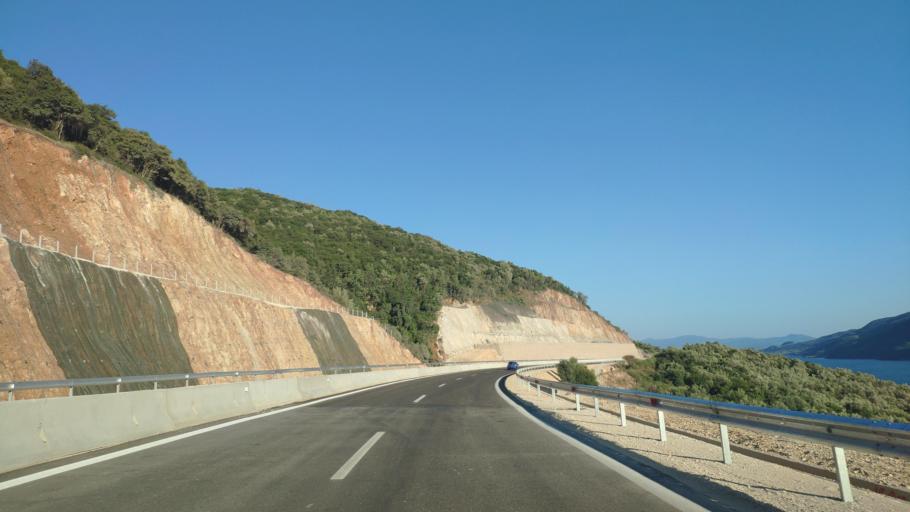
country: GR
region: West Greece
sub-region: Nomos Aitolias kai Akarnanias
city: Stanos
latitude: 38.7769
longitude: 21.1541
